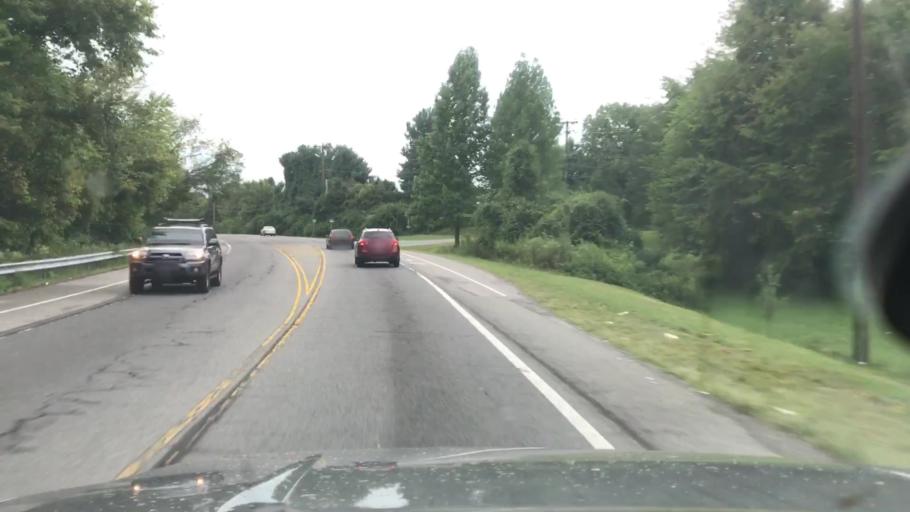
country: US
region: Tennessee
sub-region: Davidson County
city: Lakewood
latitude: 36.1359
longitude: -86.6300
